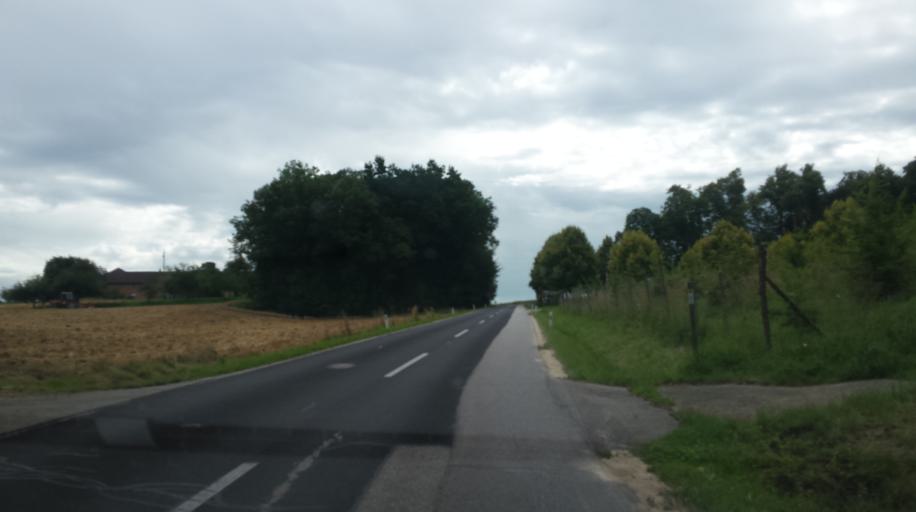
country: AT
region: Upper Austria
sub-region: Wels-Land
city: Bad Wimsbach-Neydharting
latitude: 48.0720
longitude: 13.9220
